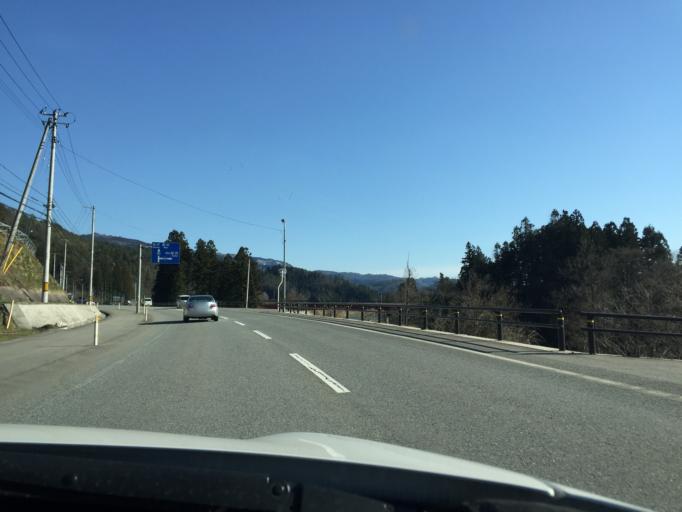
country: JP
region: Yamagata
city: Nagai
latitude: 38.2063
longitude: 140.1016
